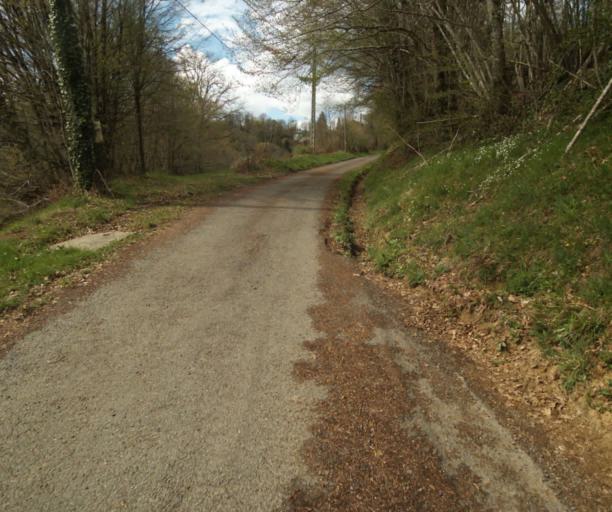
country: FR
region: Limousin
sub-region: Departement de la Correze
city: Tulle
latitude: 45.2728
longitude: 1.7944
